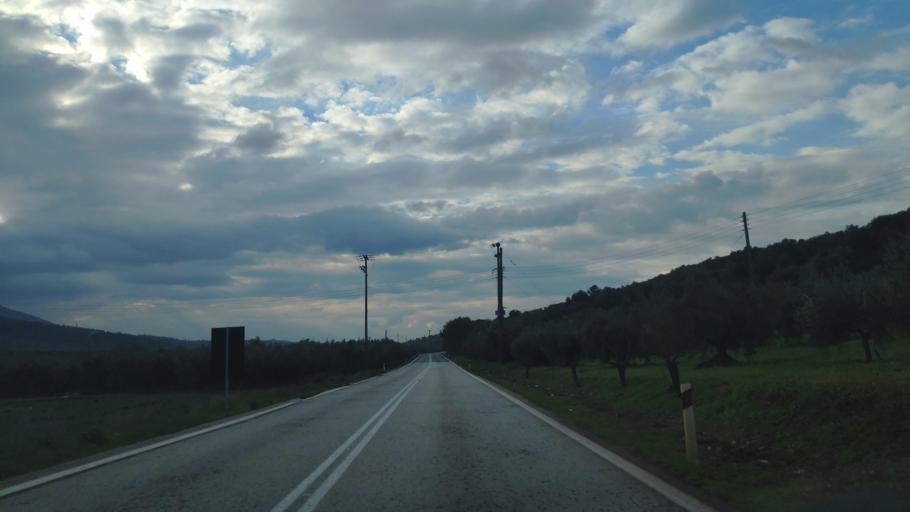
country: GR
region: Peloponnese
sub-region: Nomos Argolidos
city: Koutsopodi
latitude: 37.7475
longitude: 22.7341
